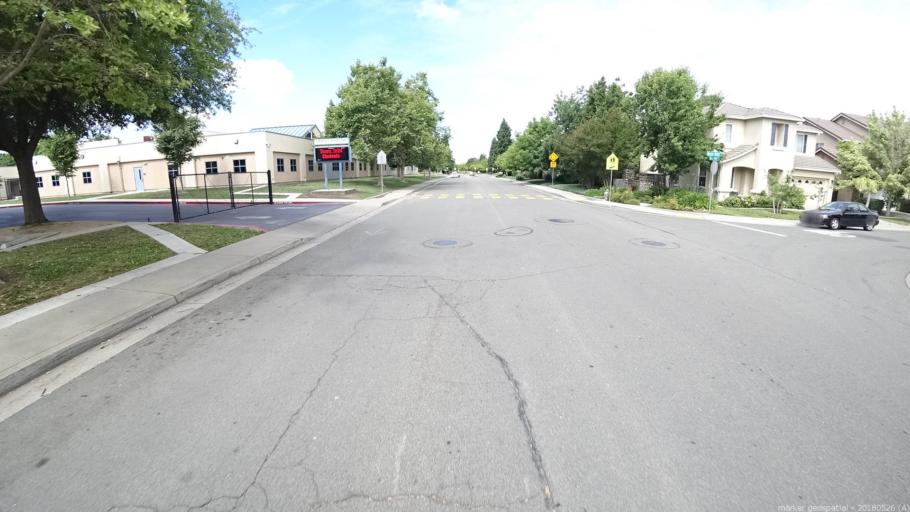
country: US
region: California
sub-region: Yolo County
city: West Sacramento
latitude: 38.6113
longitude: -121.5285
